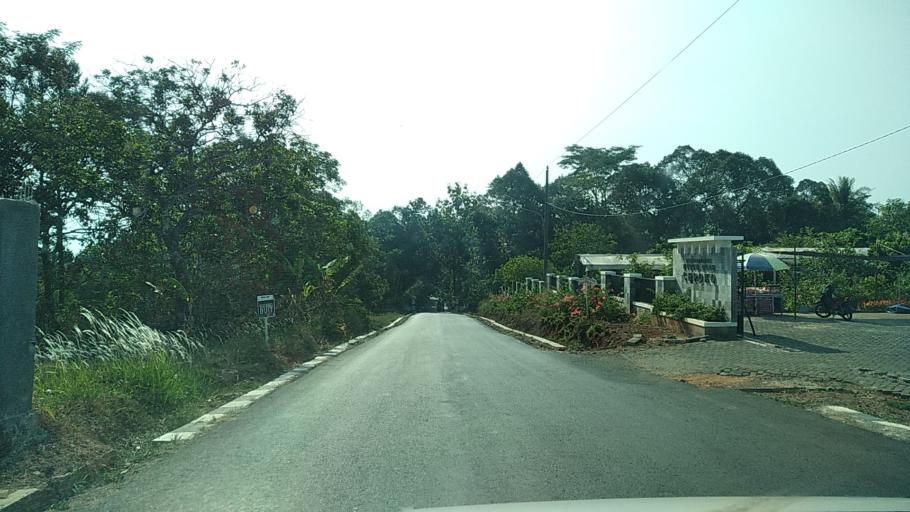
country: ID
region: Central Java
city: Ungaran
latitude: -7.0737
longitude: 110.3565
